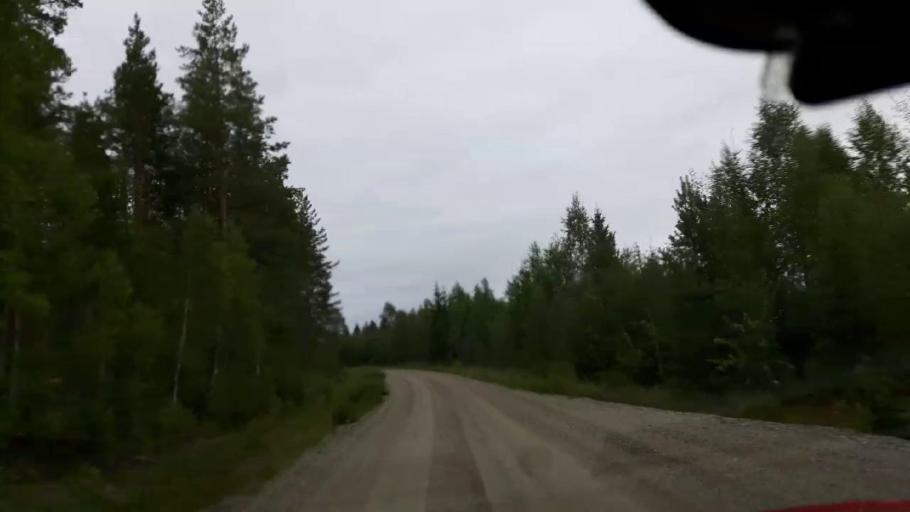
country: SE
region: Vaesternorrland
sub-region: Ange Kommun
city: Ange
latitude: 62.8042
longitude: 15.7499
